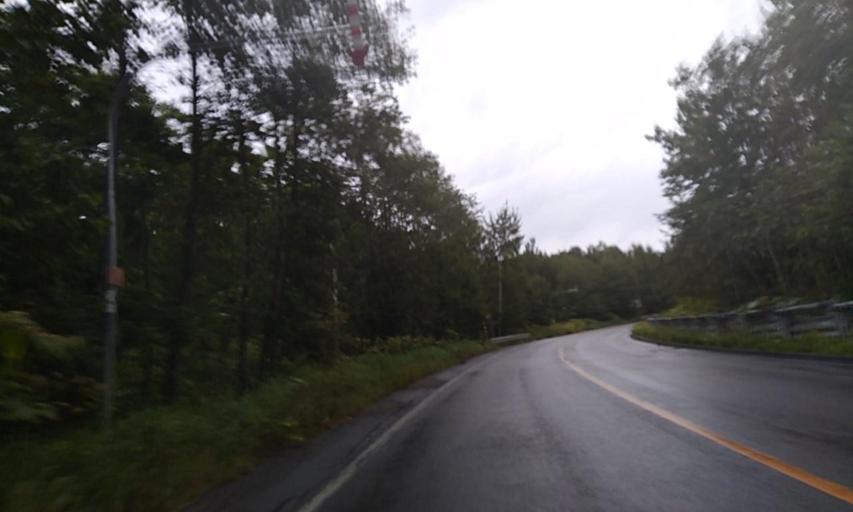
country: JP
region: Hokkaido
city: Mombetsu
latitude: 44.4886
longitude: 143.0912
